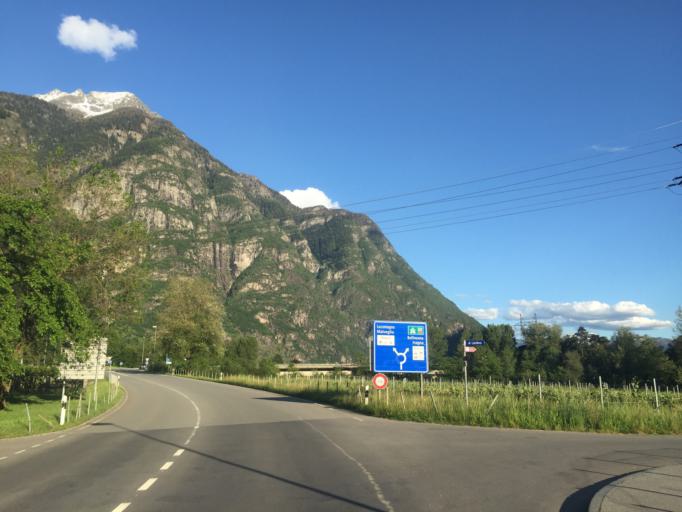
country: CH
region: Ticino
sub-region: Riviera District
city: Biasca
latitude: 46.3593
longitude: 8.9561
